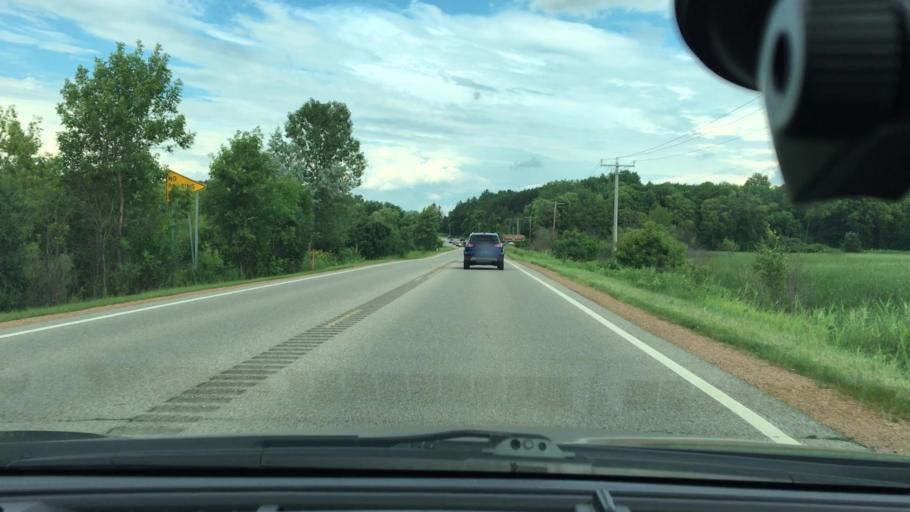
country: US
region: Minnesota
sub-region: Hennepin County
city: Shorewood
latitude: 44.8650
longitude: -93.6131
